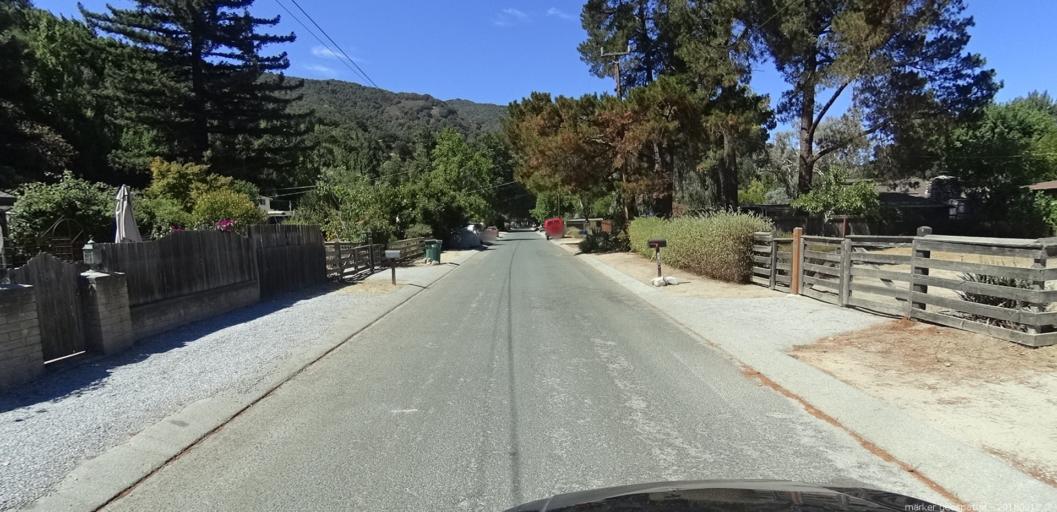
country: US
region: California
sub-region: Monterey County
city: Carmel Valley Village
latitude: 36.4737
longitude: -121.7294
